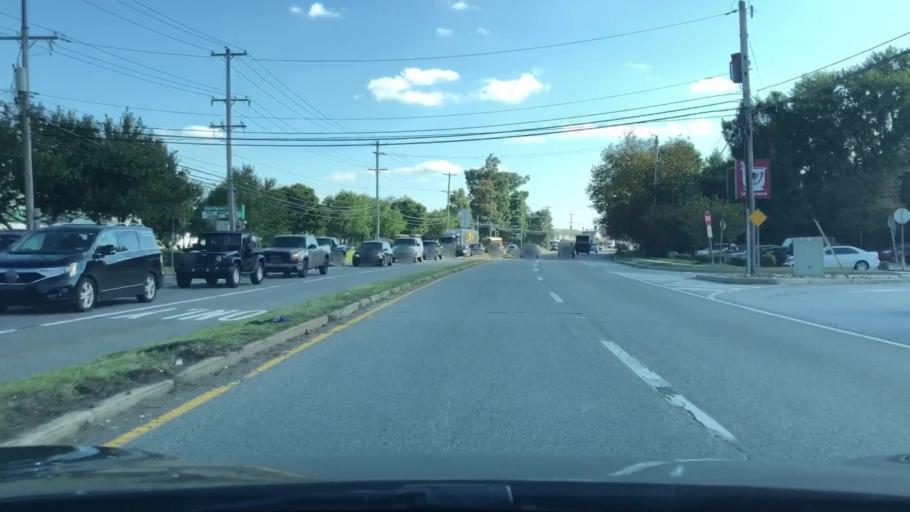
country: US
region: Pennsylvania
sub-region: Delaware County
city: Chester Heights
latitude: 39.8492
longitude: -75.5380
